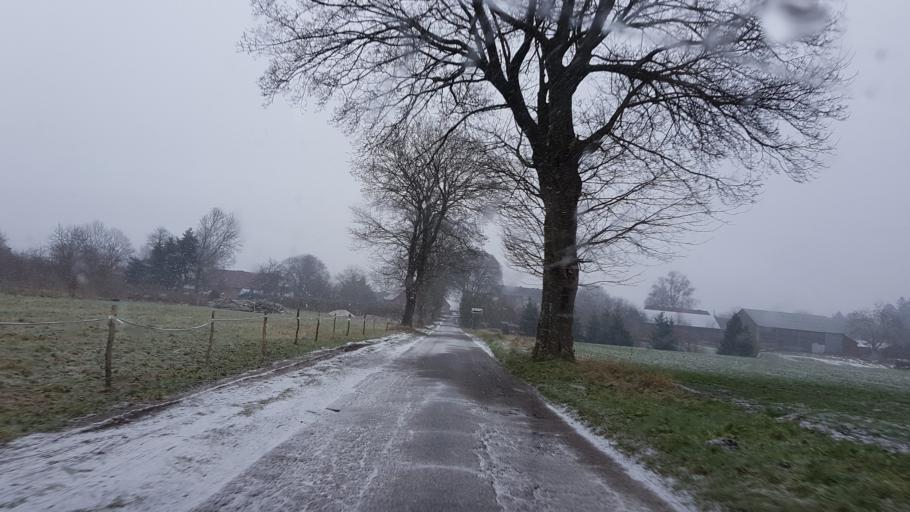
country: PL
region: West Pomeranian Voivodeship
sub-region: Powiat slawienski
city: Slawno
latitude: 54.2752
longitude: 16.6314
